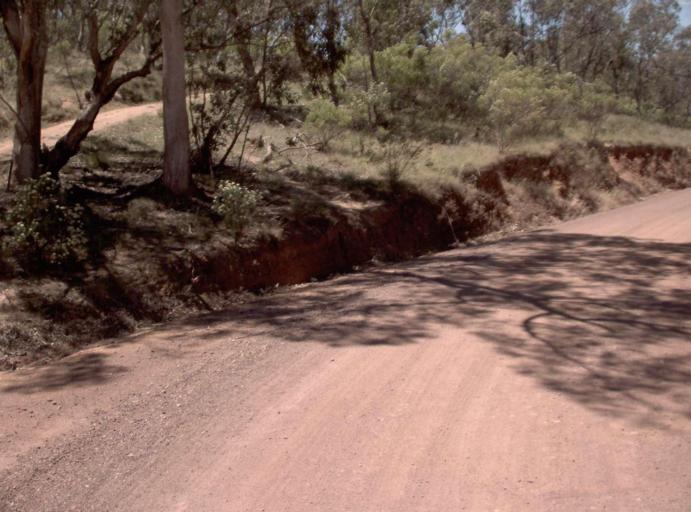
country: AU
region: New South Wales
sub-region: Snowy River
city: Jindabyne
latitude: -36.9355
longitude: 148.3447
